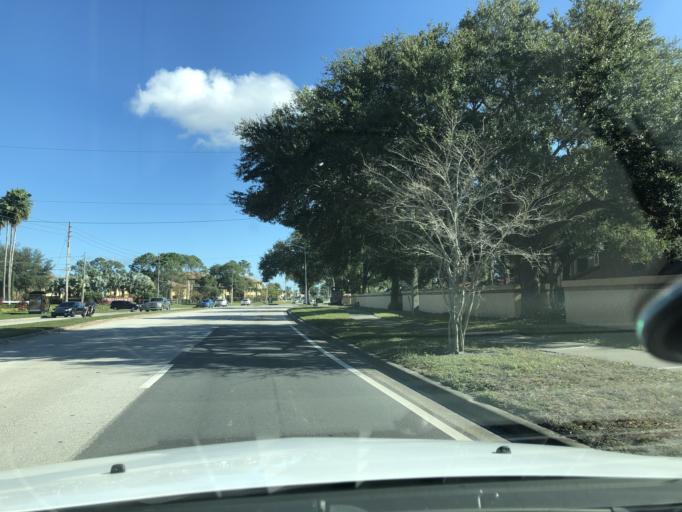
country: US
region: Florida
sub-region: Orange County
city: Oak Ridge
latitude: 28.4969
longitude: -81.4403
